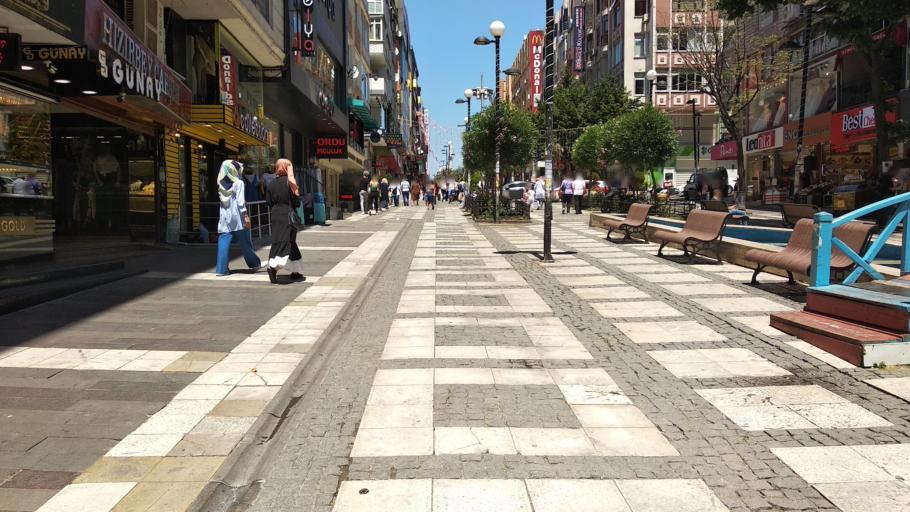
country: TR
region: Istanbul
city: Yakuplu
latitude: 40.9803
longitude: 28.7219
